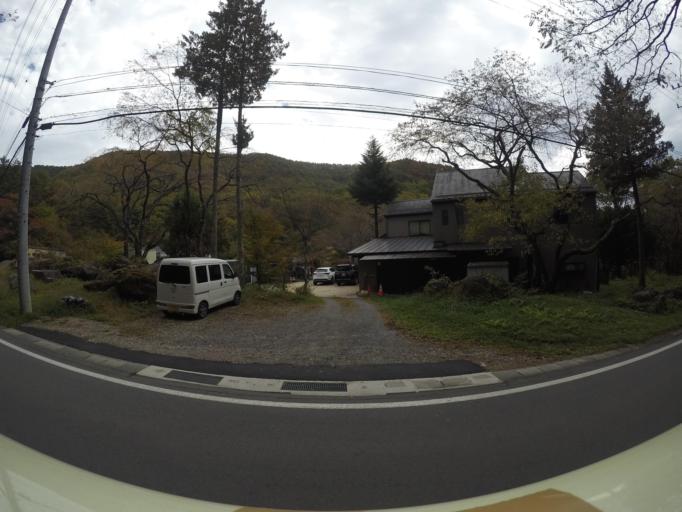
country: JP
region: Nagano
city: Chino
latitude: 35.9610
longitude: 138.1134
